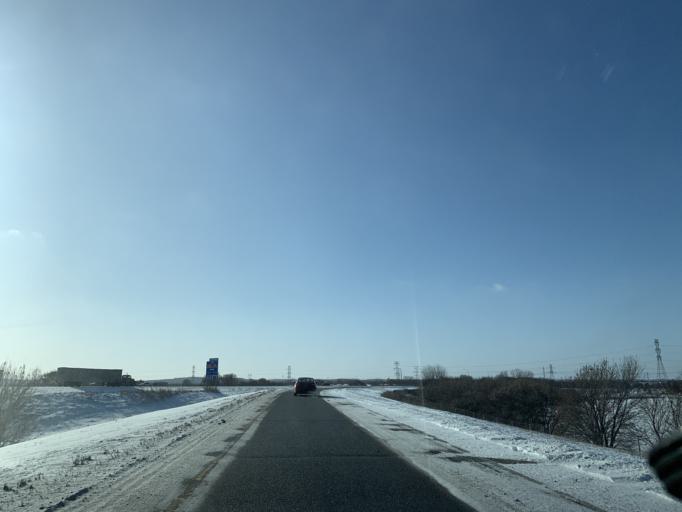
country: US
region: Minnesota
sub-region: Scott County
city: Prior Lake
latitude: 44.7863
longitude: -93.4163
